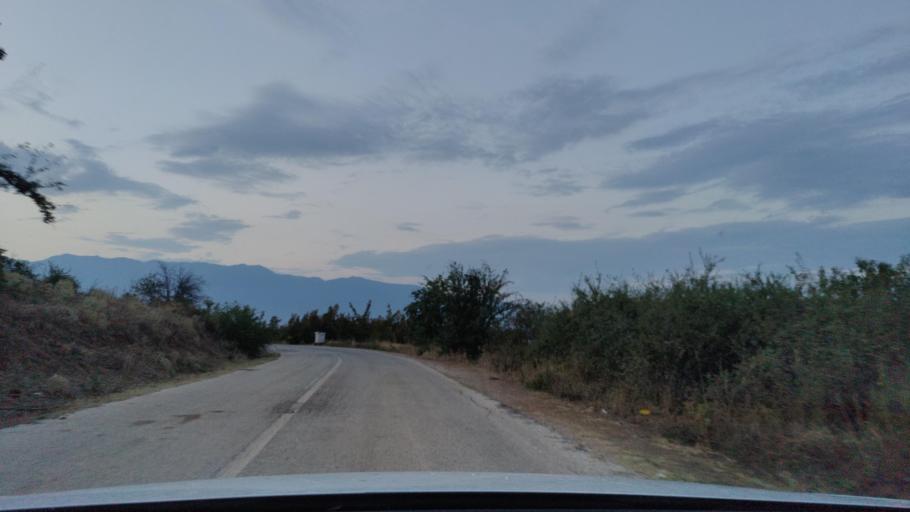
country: GR
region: Central Macedonia
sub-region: Nomos Serron
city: Chrysochorafa
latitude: 41.1503
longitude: 23.2060
